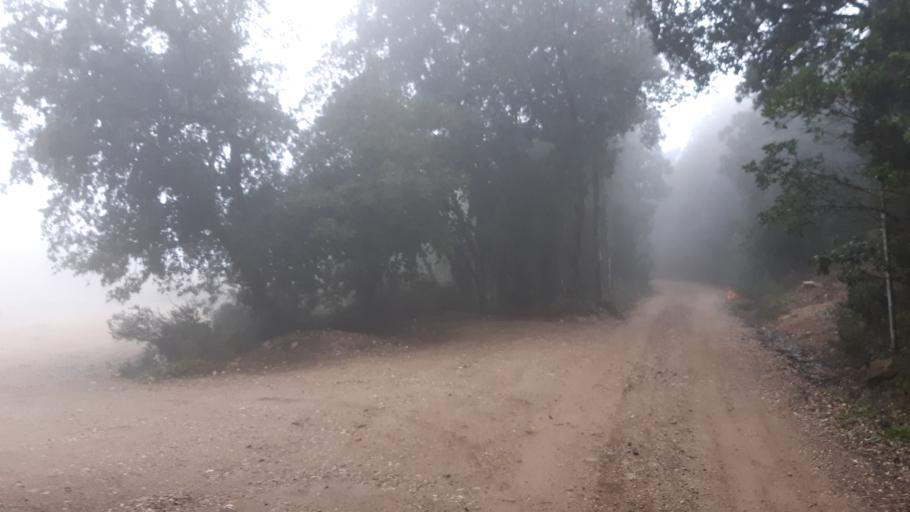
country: IT
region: Sardinia
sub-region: Provincia di Carbonia-Iglesias
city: Fluminimaggiore
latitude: 39.3951
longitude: 8.5657
